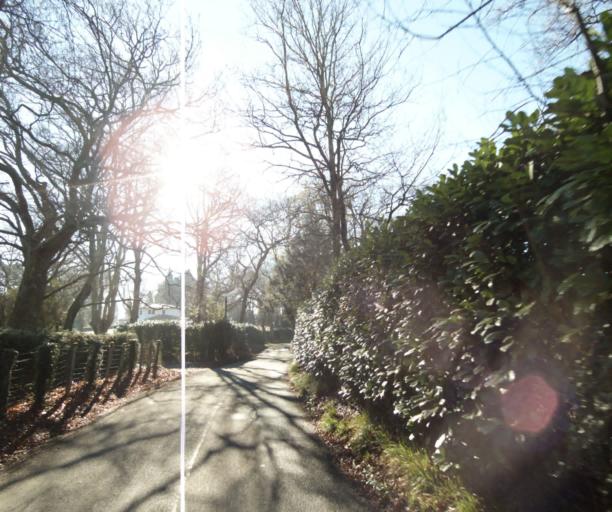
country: FR
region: Aquitaine
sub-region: Departement des Pyrenees-Atlantiques
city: Ciboure
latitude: 43.3657
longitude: -1.6615
